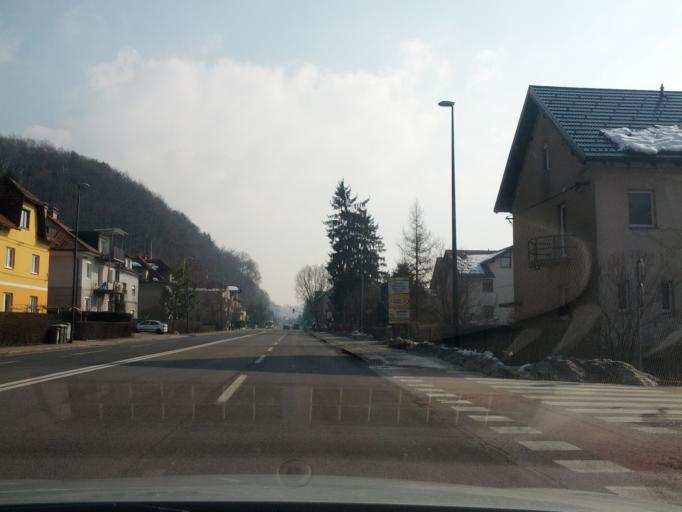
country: SI
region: Ljubljana
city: Ljubljana
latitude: 46.0331
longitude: 14.5277
